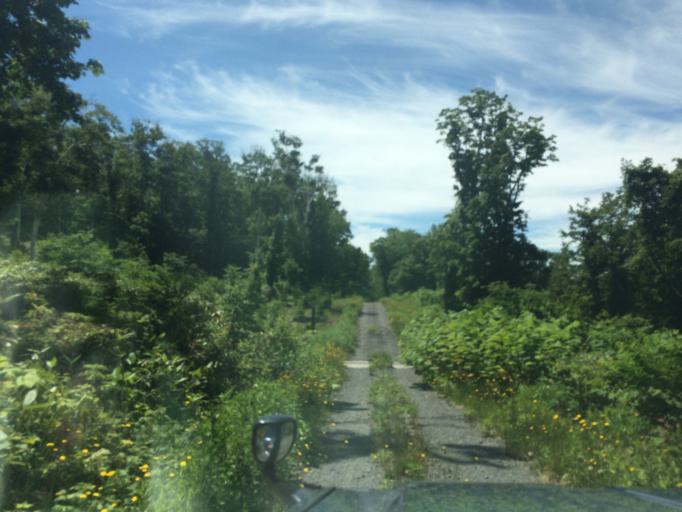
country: JP
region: Hokkaido
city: Niseko Town
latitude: 42.8656
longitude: 140.8151
